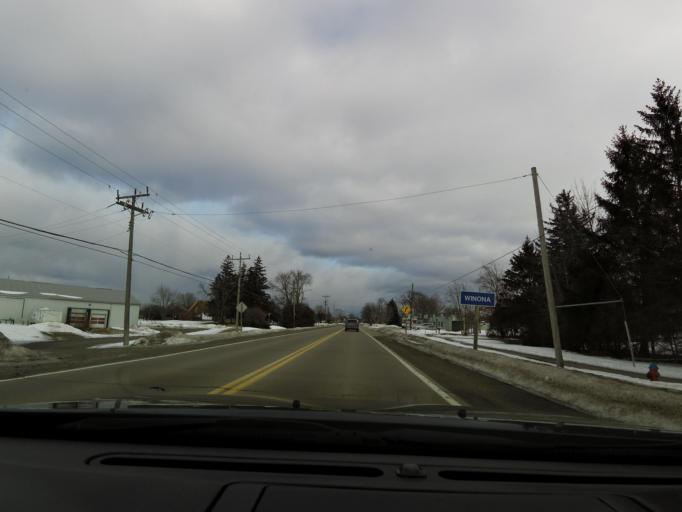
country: CA
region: Ontario
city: Hamilton
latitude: 43.2081
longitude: -79.6706
